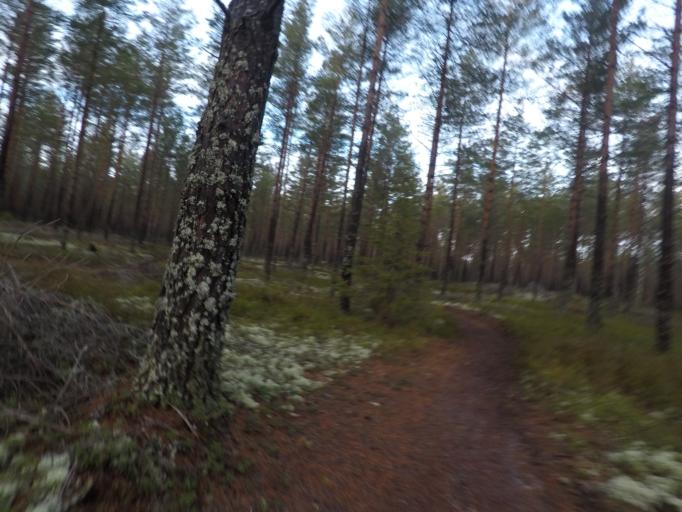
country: SE
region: Vaestmanland
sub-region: Kungsors Kommun
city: Kungsoer
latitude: 59.3502
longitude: 16.1195
